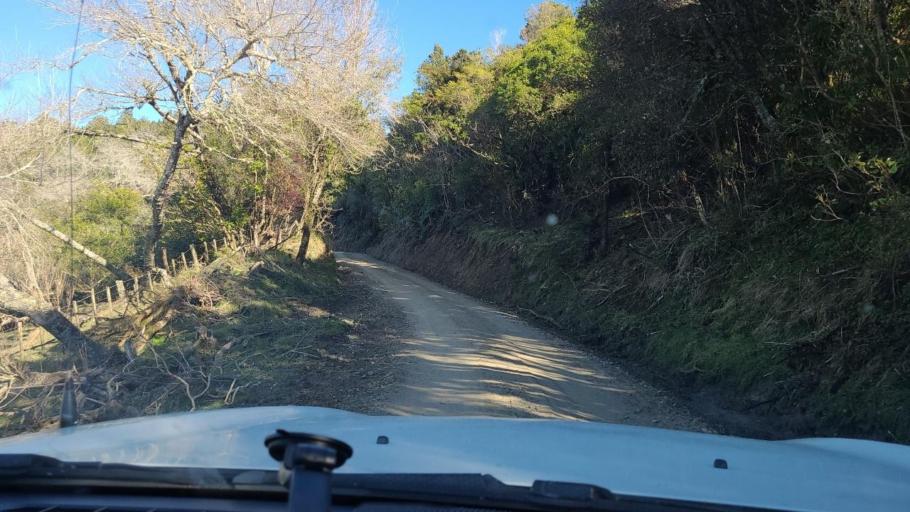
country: NZ
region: Hawke's Bay
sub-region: Wairoa District
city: Wairoa
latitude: -38.6783
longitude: 177.4694
